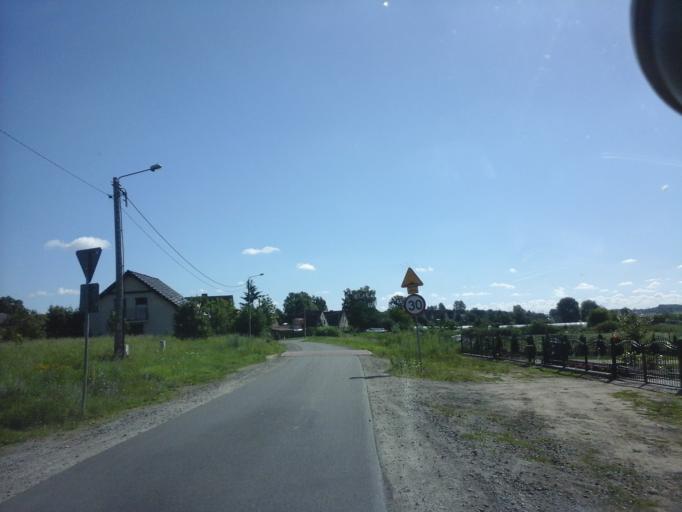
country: PL
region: West Pomeranian Voivodeship
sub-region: Powiat choszczenski
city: Choszczno
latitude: 53.1802
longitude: 15.4228
